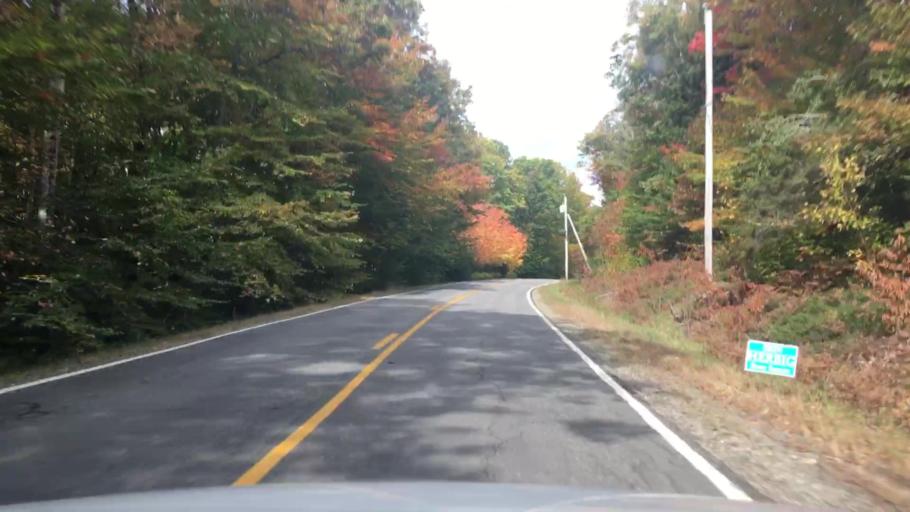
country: US
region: Maine
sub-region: Knox County
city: Hope
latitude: 44.3185
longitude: -69.1250
